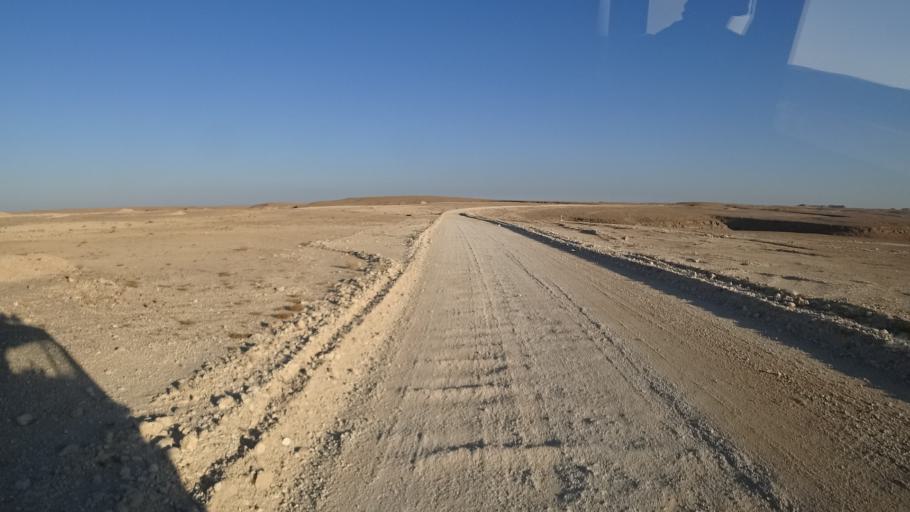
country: YE
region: Al Mahrah
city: Hawf
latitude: 17.1870
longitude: 53.3402
